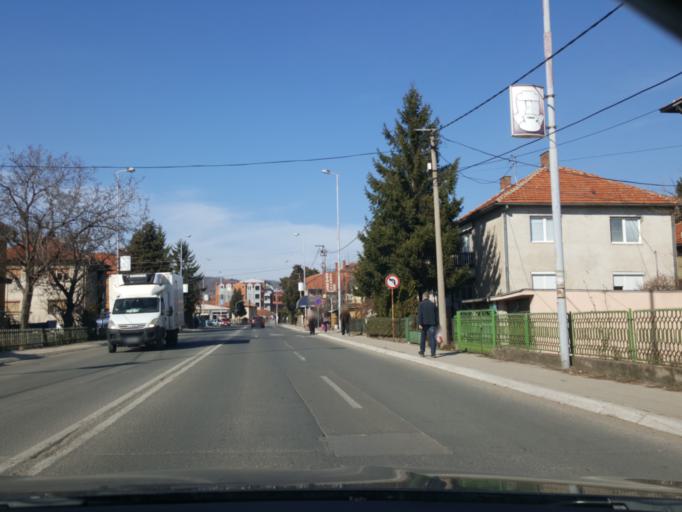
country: RS
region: Central Serbia
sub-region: Nisavski Okrug
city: Nis
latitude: 43.3282
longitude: 21.9253
